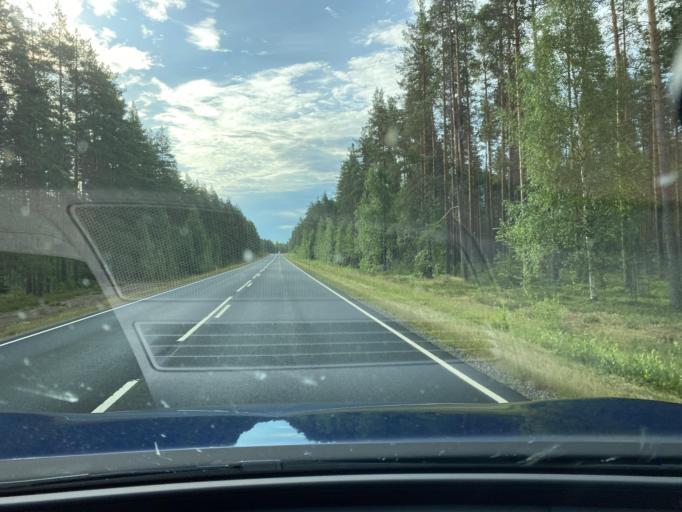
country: FI
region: Central Ostrobothnia
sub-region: Kaustinen
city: Veteli
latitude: 63.4098
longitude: 23.9652
